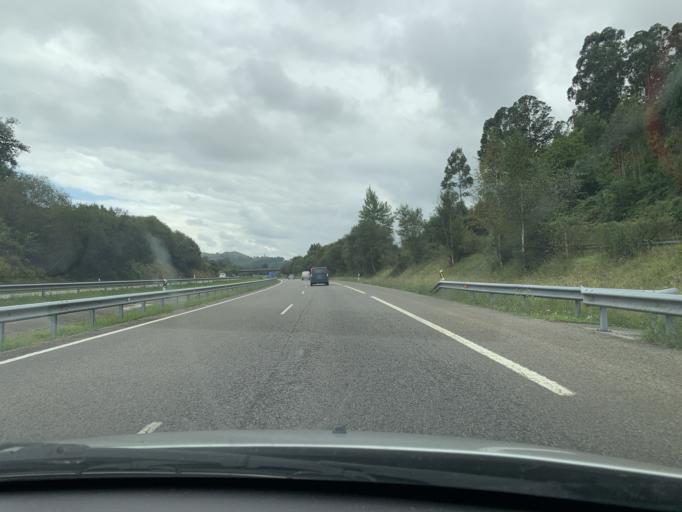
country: ES
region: Asturias
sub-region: Province of Asturias
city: Llanes
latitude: 43.4123
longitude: -4.7828
